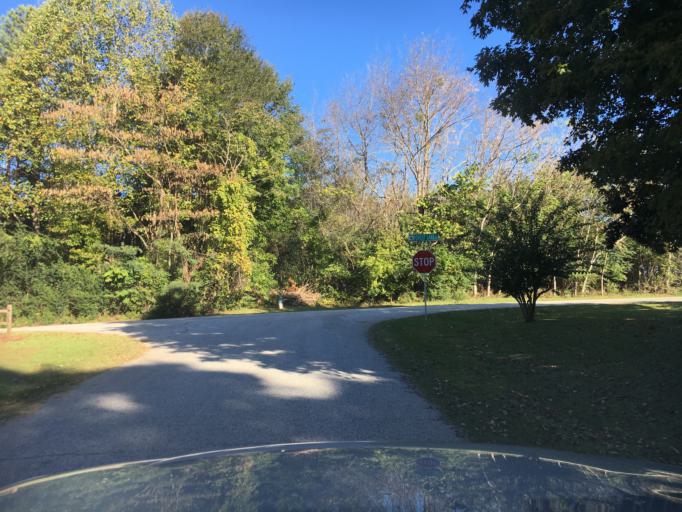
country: US
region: South Carolina
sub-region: Spartanburg County
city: Lyman
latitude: 34.9262
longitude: -82.1235
